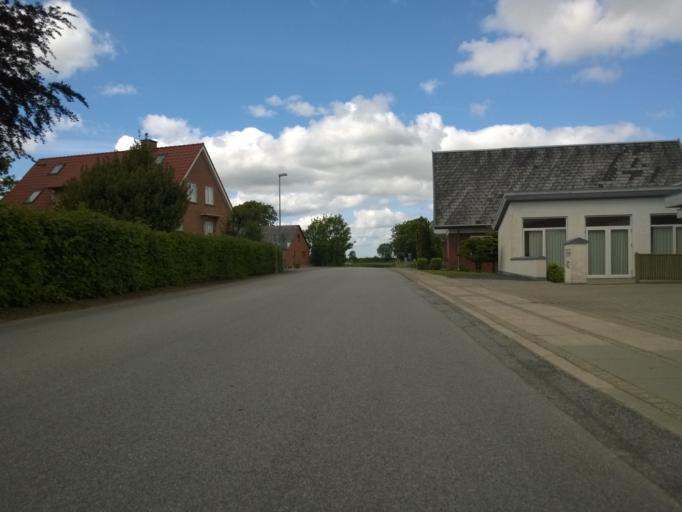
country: DK
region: Central Jutland
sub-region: Holstebro Kommune
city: Vinderup
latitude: 56.4073
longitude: 8.7526
